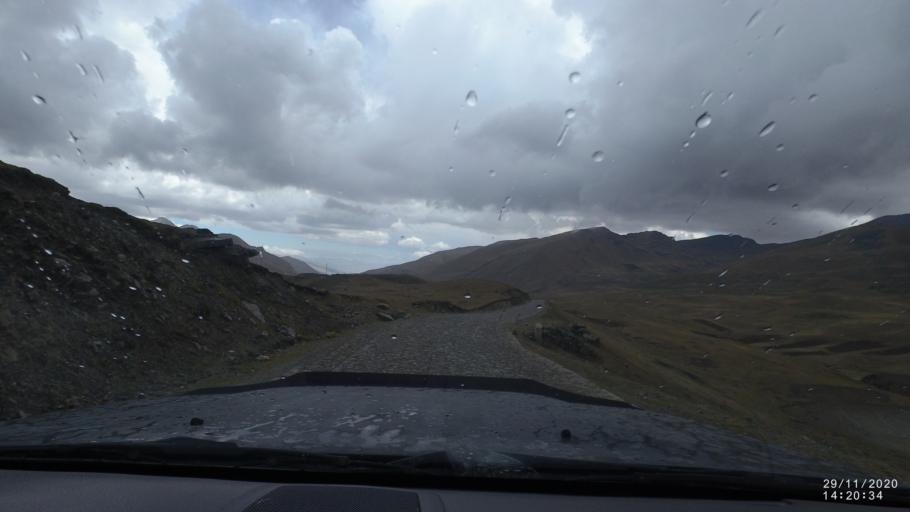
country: BO
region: Cochabamba
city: Sipe Sipe
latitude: -17.2492
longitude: -66.3924
